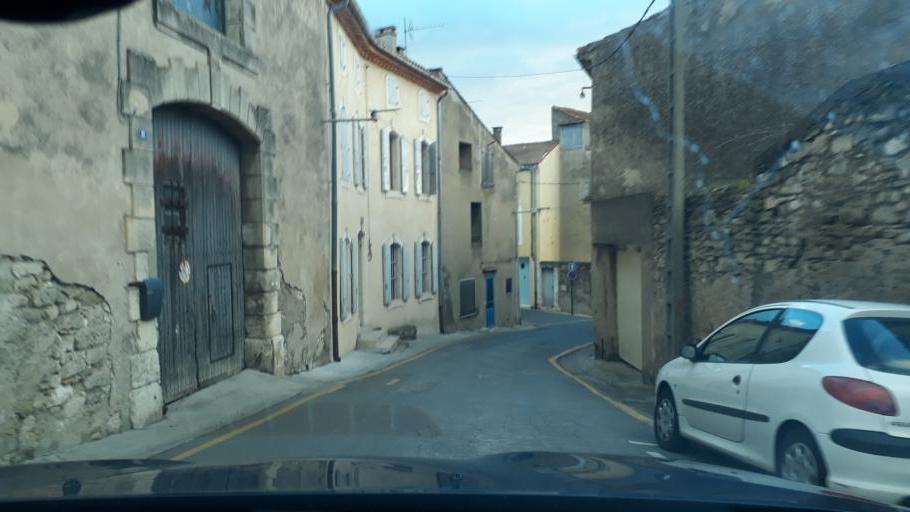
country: FR
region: Languedoc-Roussillon
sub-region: Departement de l'Herault
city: Nissan-lez-Enserune
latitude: 43.2906
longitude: 3.1295
